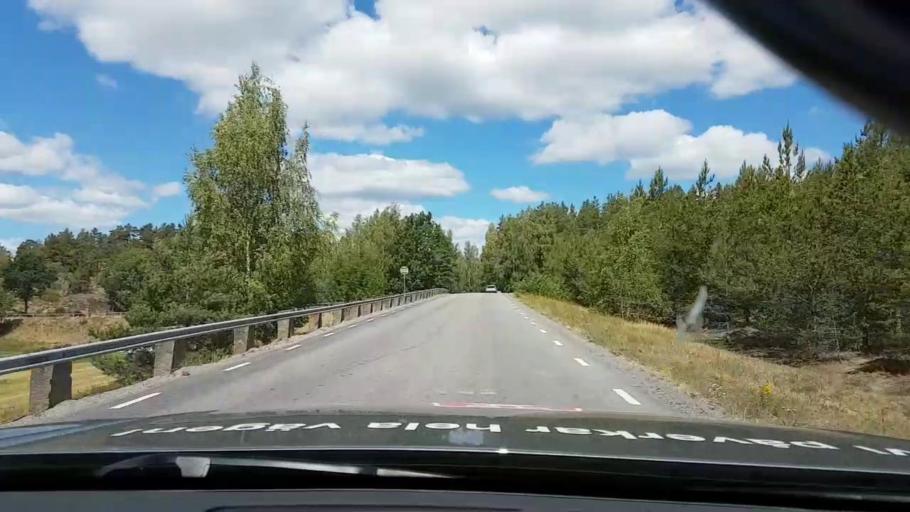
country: SE
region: Kalmar
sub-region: Vasterviks Kommun
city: Forserum
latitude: 58.0239
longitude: 16.5731
